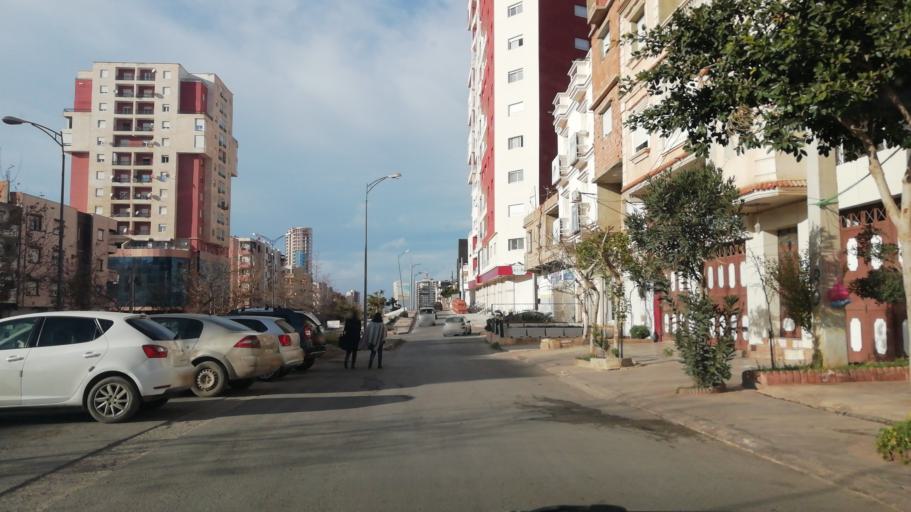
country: DZ
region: Oran
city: Bir el Djir
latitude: 35.7224
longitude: -0.5836
